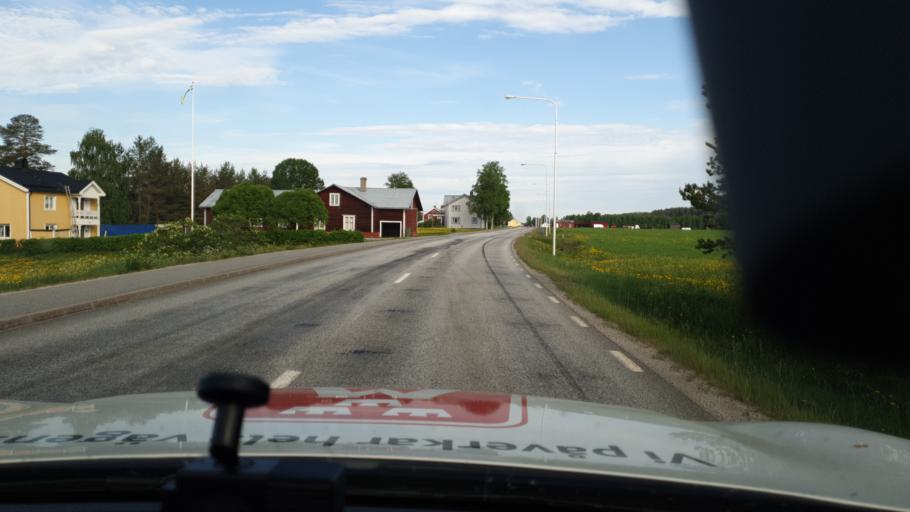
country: SE
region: Vaesterbotten
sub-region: Bjurholms Kommun
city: Bjurholm
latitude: 64.2555
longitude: 19.2969
